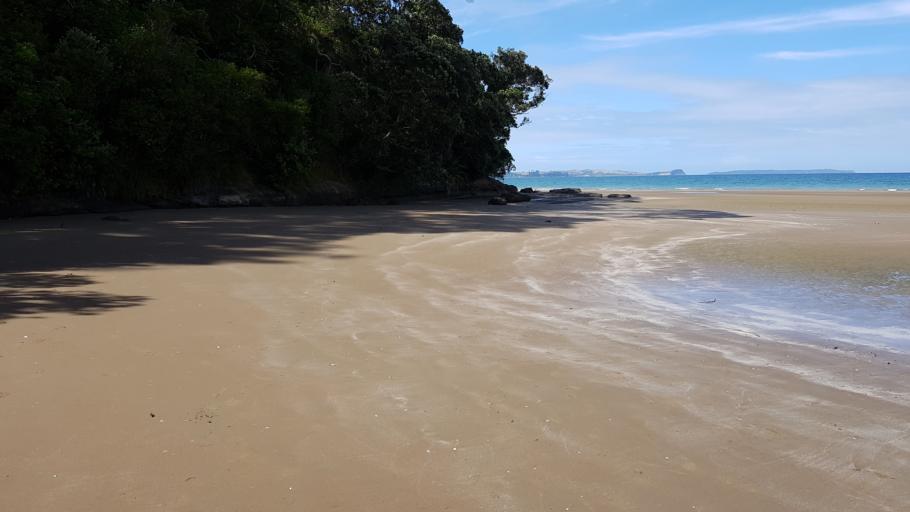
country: NZ
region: Auckland
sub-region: Auckland
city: Rothesay Bay
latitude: -36.6794
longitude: 174.7479
